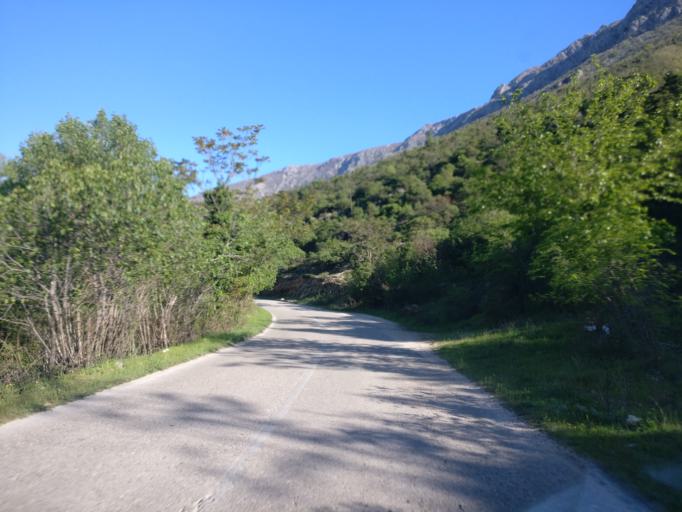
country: BA
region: Federation of Bosnia and Herzegovina
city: Stolac
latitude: 43.0857
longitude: 18.0047
